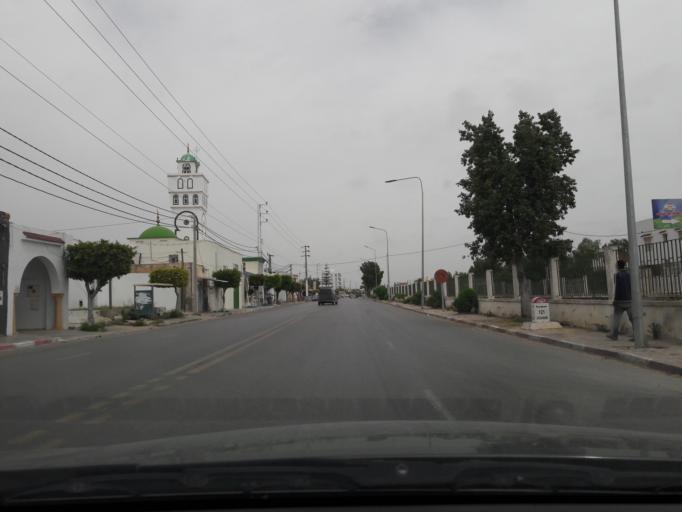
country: TN
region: Safaqis
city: Al Qarmadah
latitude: 34.7870
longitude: 10.7602
